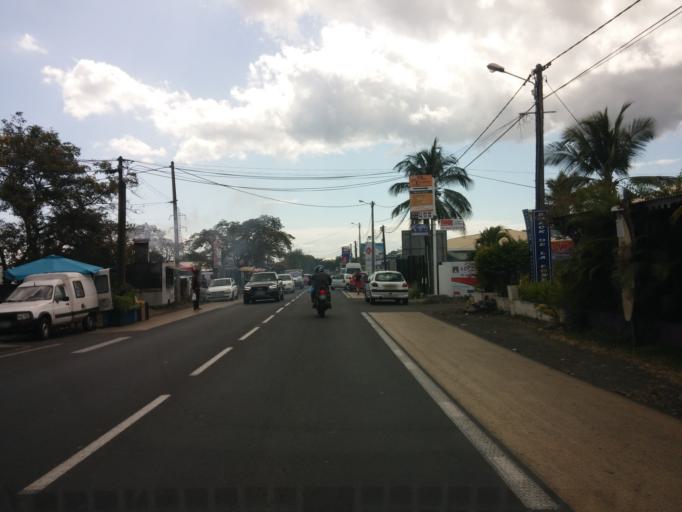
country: RE
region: Reunion
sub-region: Reunion
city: La Possession
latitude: -20.9443
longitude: 55.3286
